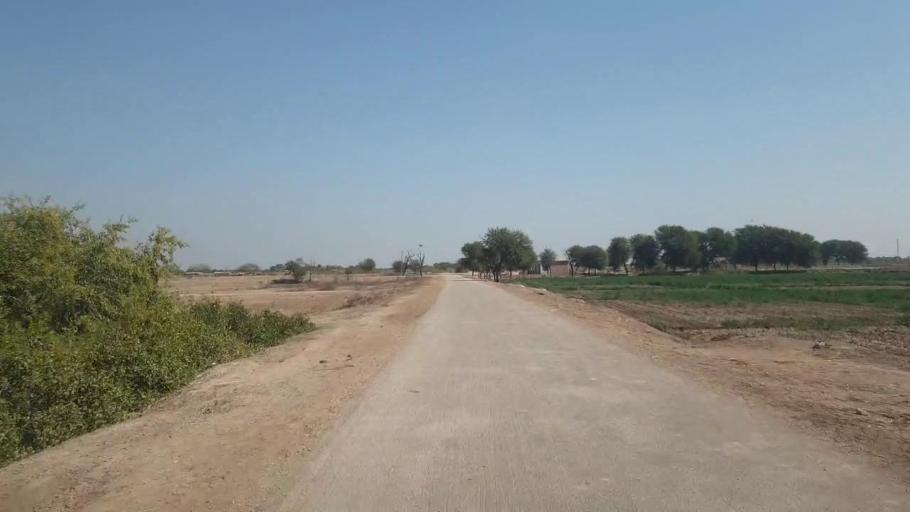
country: PK
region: Sindh
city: Chambar
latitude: 25.2886
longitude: 68.6896
